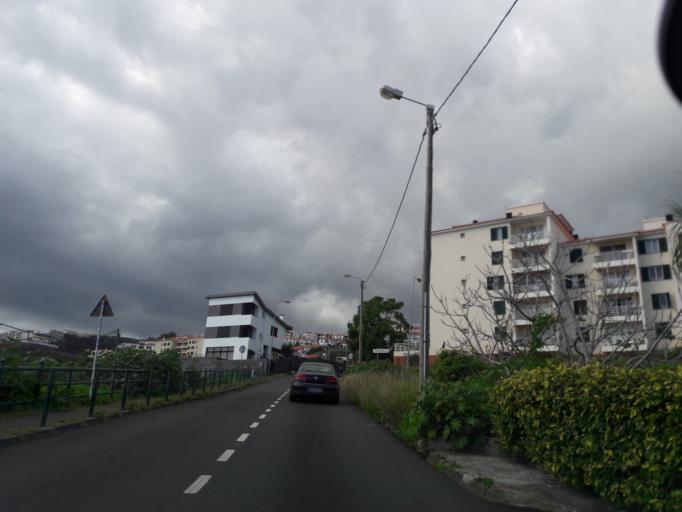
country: PT
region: Madeira
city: Canico
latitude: 32.6457
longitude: -16.8358
